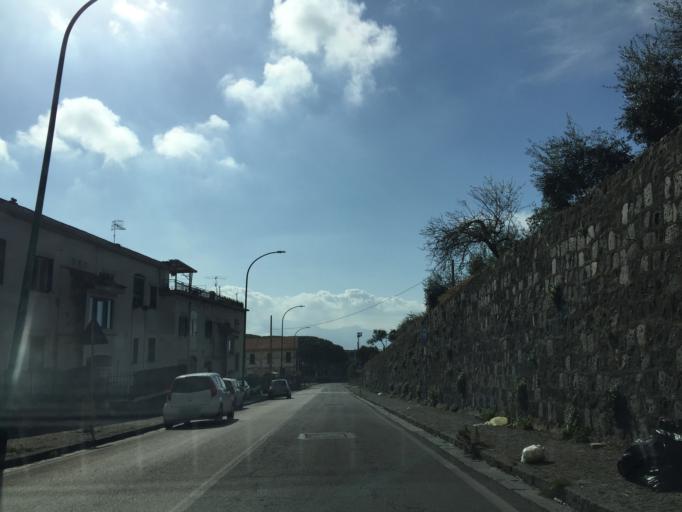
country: IT
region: Campania
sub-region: Provincia di Napoli
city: Torre del Greco
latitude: 40.7810
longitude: 14.4082
